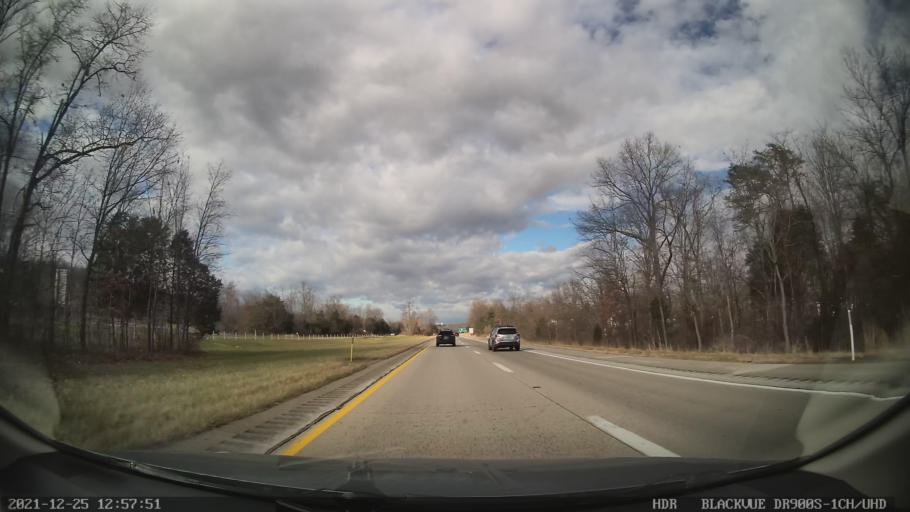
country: US
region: Pennsylvania
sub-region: Adams County
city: Lake Heritage
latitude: 39.8162
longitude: -77.1955
